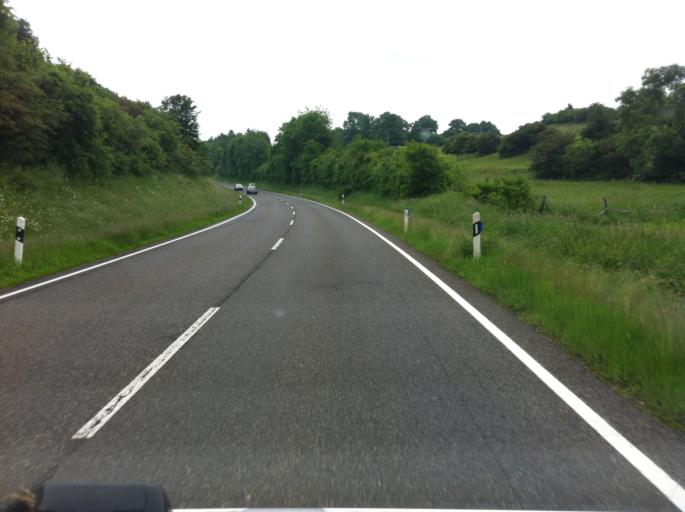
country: DE
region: North Rhine-Westphalia
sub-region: Regierungsbezirk Koln
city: Nettersheim
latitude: 50.4982
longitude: 6.6298
